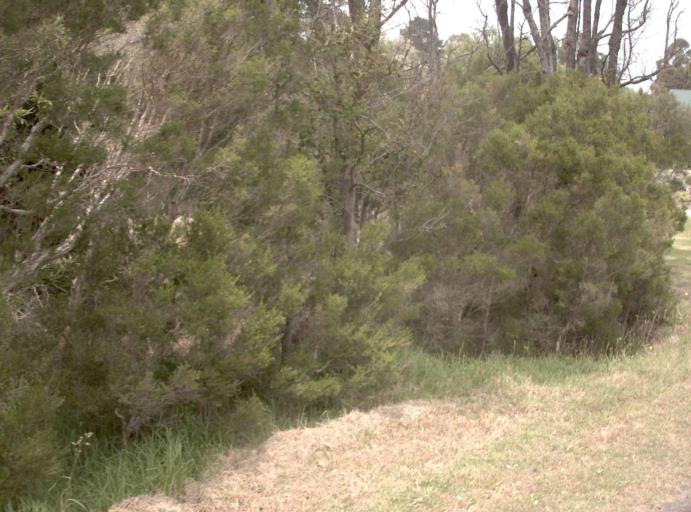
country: AU
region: Victoria
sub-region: Latrobe
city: Traralgon
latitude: -38.4716
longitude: 146.7173
